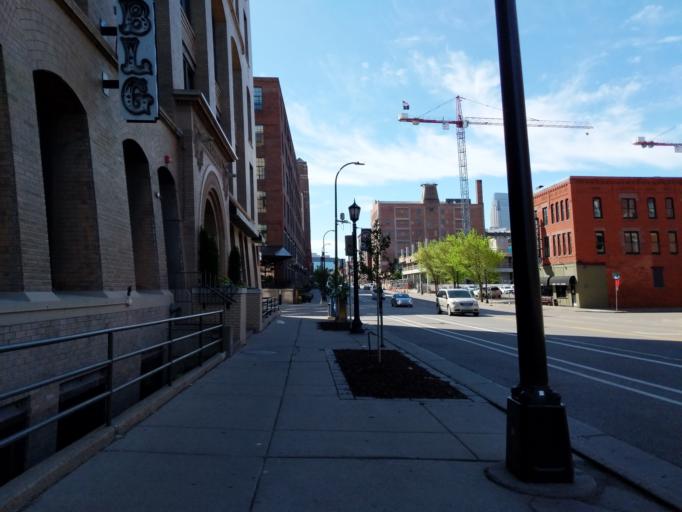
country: US
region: Minnesota
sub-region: Hennepin County
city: Minneapolis
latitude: 44.9892
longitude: -93.2789
